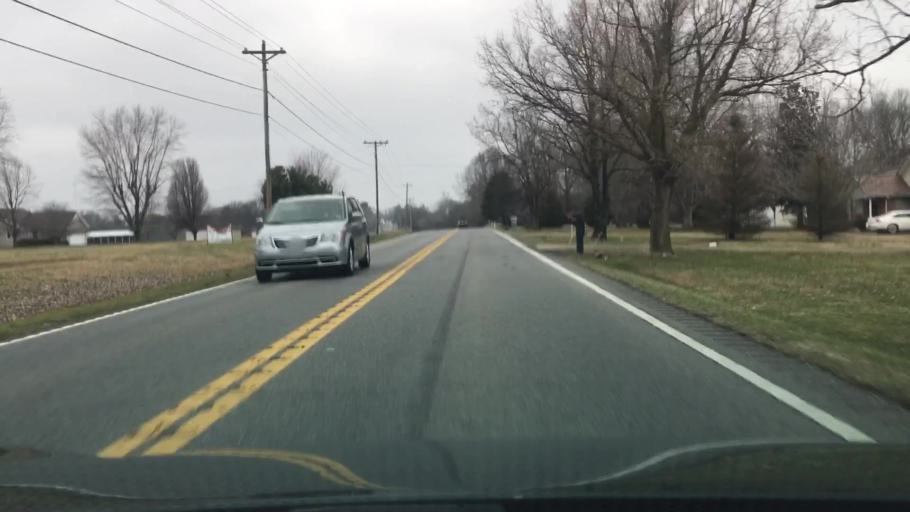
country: US
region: Kentucky
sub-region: Marshall County
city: Calvert City
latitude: 36.9540
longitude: -88.3709
